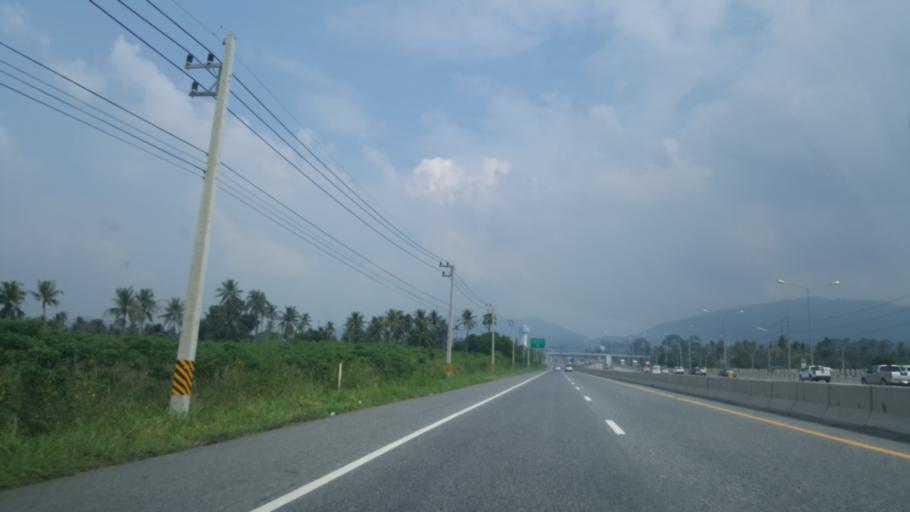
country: TH
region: Chon Buri
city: Si Racha
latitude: 13.2028
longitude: 101.0023
